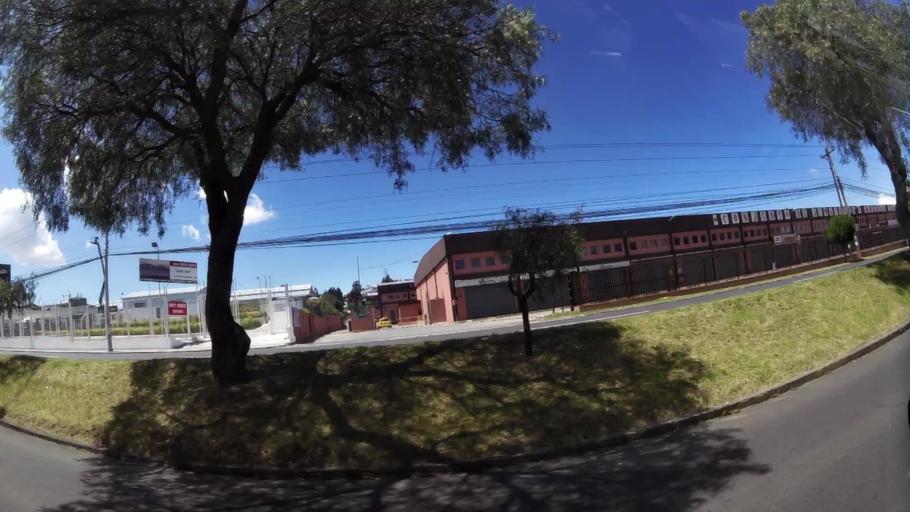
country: EC
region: Pichincha
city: Quito
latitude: -0.1089
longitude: -78.4781
